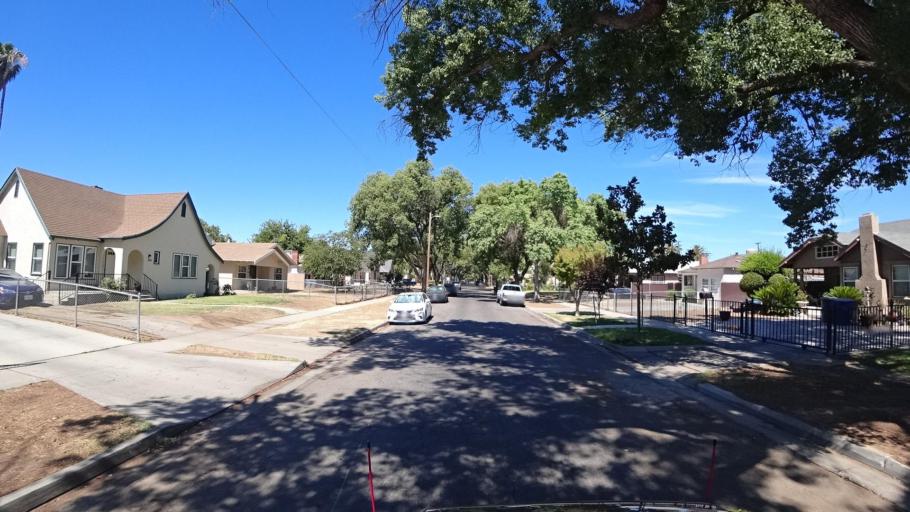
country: US
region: California
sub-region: Fresno County
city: Fresno
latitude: 36.7459
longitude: -119.7490
